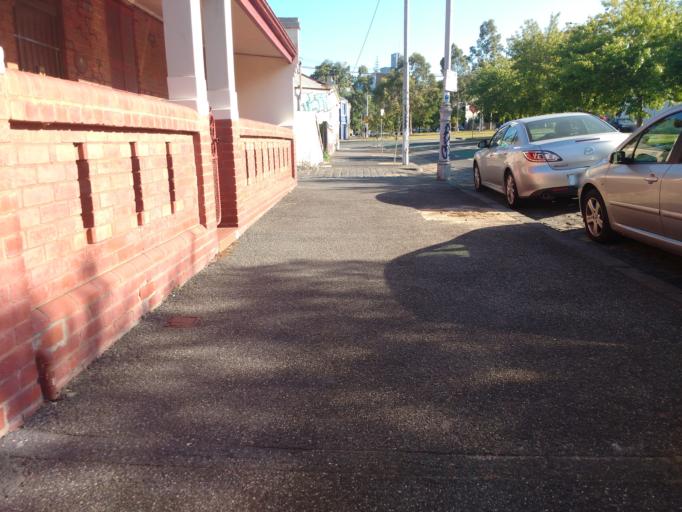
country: AU
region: Victoria
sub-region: Yarra
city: Fitzroy
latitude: -37.7985
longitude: 144.9729
